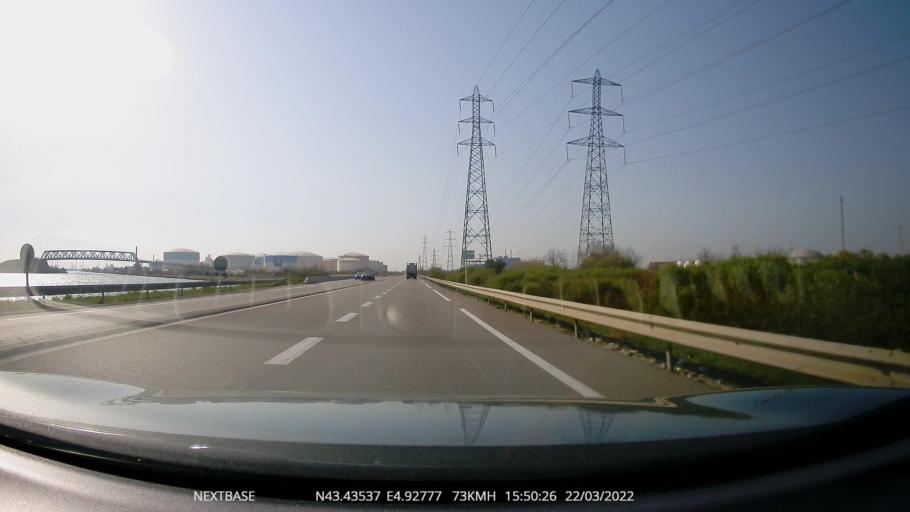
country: FR
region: Provence-Alpes-Cote d'Azur
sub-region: Departement des Bouches-du-Rhone
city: Fos-sur-Mer
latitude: 43.4354
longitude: 4.9276
